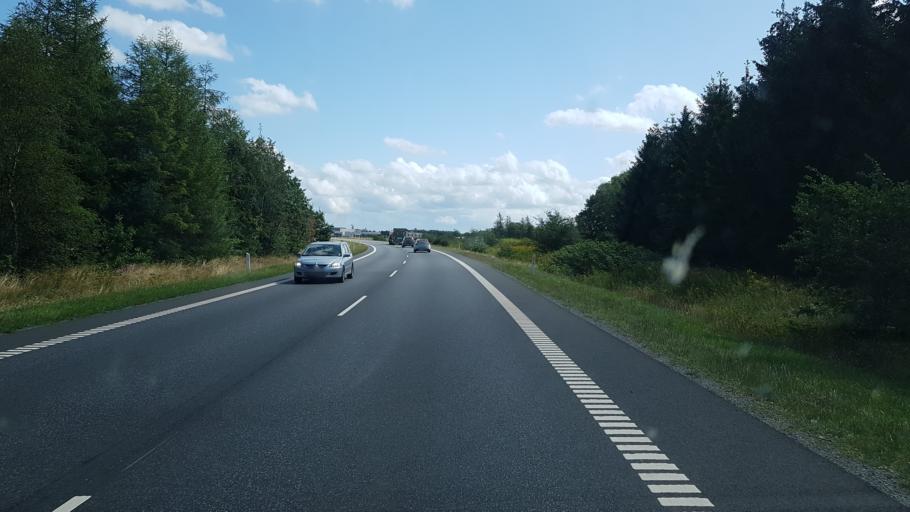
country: DK
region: South Denmark
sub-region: Billund Kommune
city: Billund
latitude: 55.7386
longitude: 9.0830
